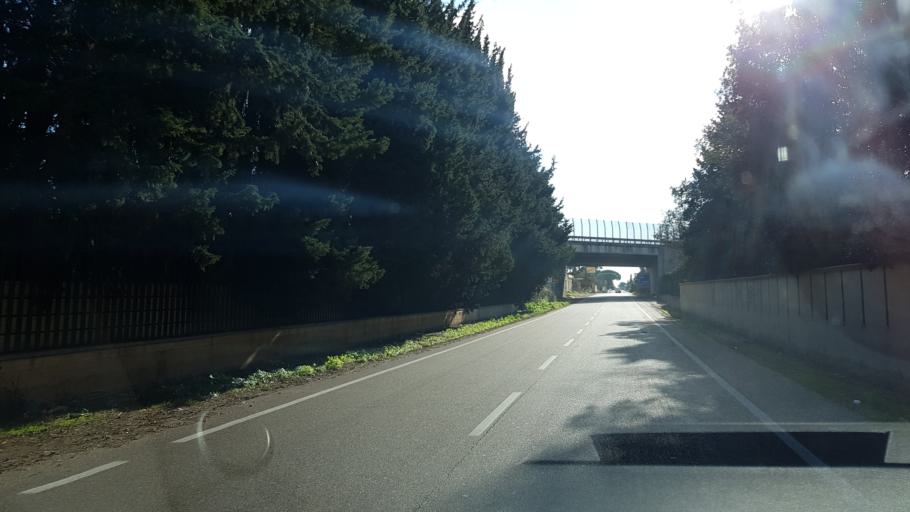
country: IT
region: Apulia
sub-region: Provincia di Lecce
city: Castromediano
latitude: 40.3269
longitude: 18.1844
